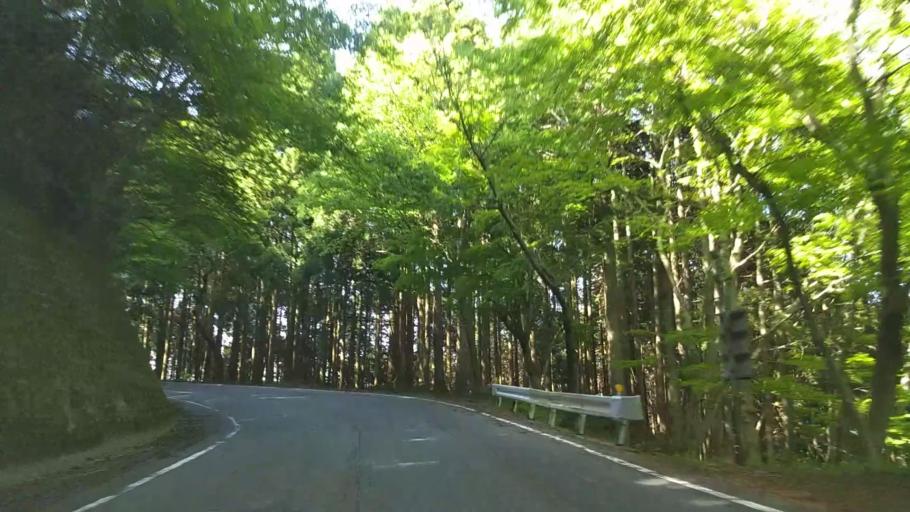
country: JP
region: Shizuoka
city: Gotemba
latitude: 35.2771
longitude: 138.9642
